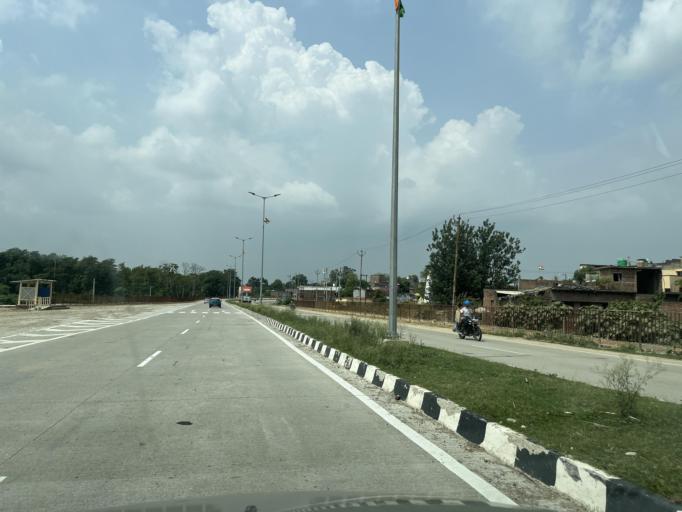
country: IN
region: Uttar Pradesh
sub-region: Bijnor
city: Sherkot
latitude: 29.3303
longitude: 78.5684
